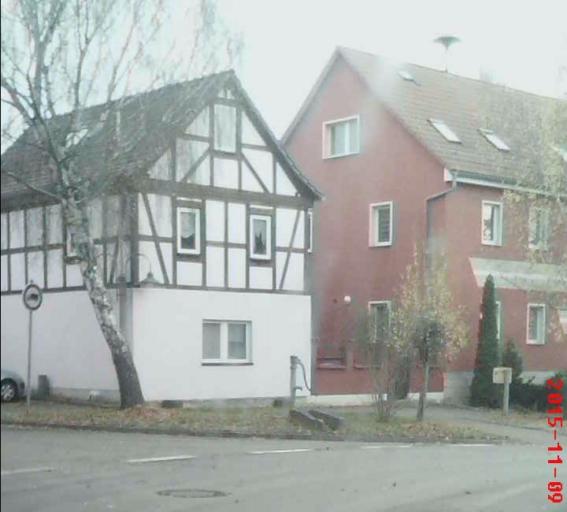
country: DE
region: Thuringia
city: Seebach
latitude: 51.1651
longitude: 10.5132
